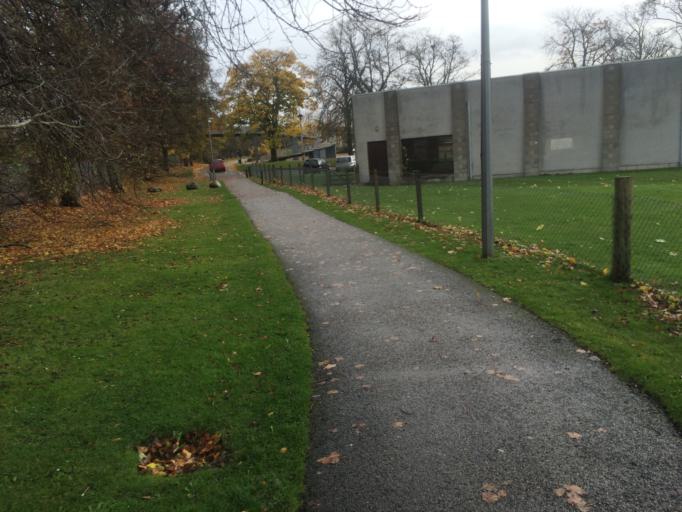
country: GB
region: Scotland
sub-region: Highland
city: Alness
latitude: 57.6944
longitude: -4.2523
